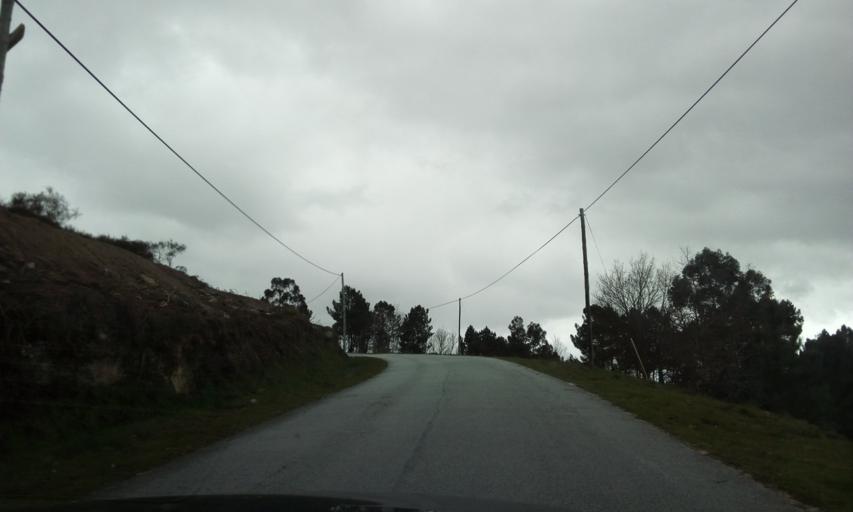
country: PT
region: Guarda
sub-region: Fornos de Algodres
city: Fornos de Algodres
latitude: 40.6369
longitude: -7.6040
